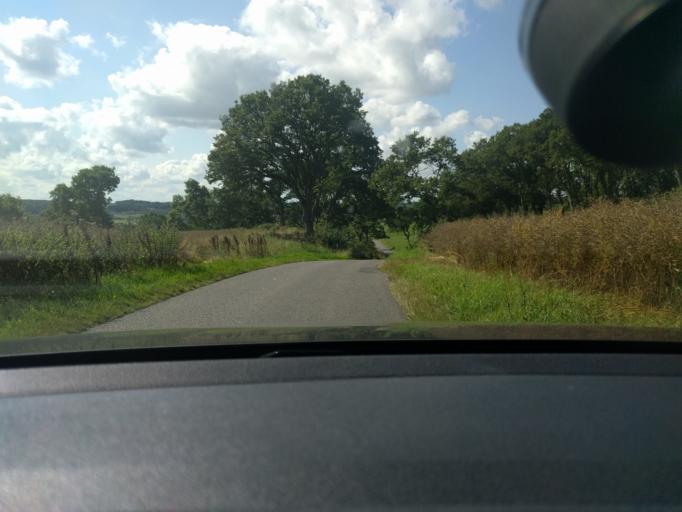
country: DK
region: Central Jutland
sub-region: Viborg Kommune
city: Bjerringbro
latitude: 56.4602
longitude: 9.5917
